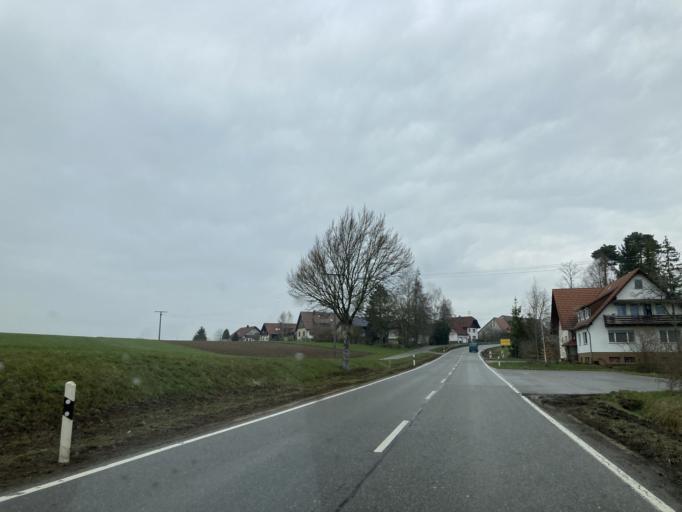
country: DE
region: Baden-Wuerttemberg
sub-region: Freiburg Region
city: Aichhalden
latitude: 48.2528
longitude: 8.4431
